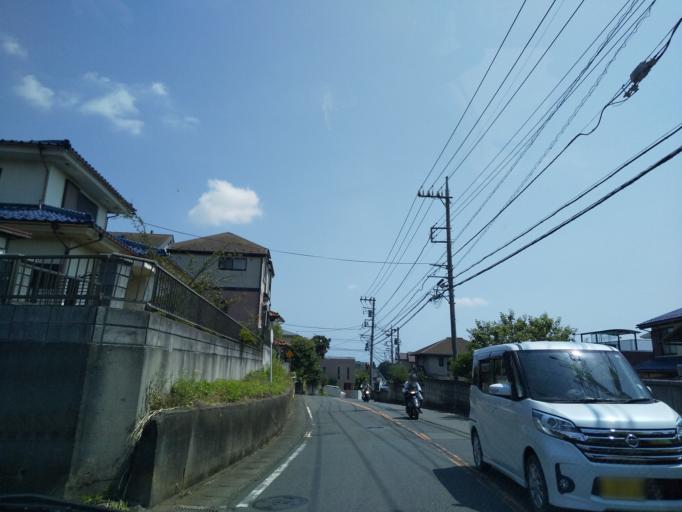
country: JP
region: Kanagawa
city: Zama
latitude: 35.5105
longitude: 139.3912
